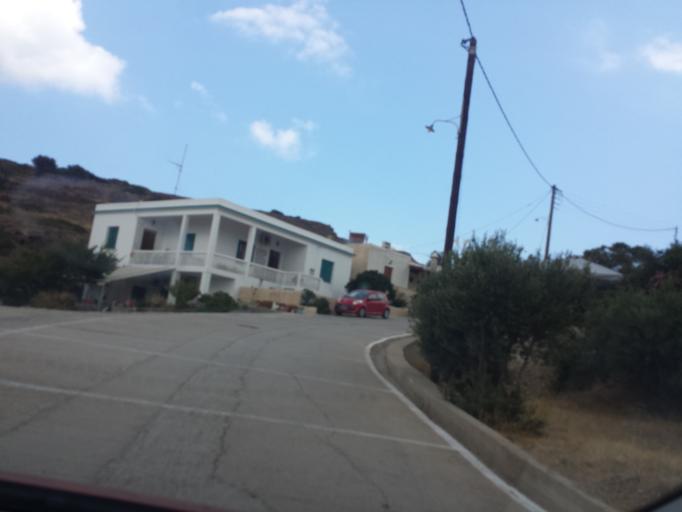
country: GR
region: South Aegean
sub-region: Nomos Kykladon
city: Milos
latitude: 36.7398
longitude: 24.4243
